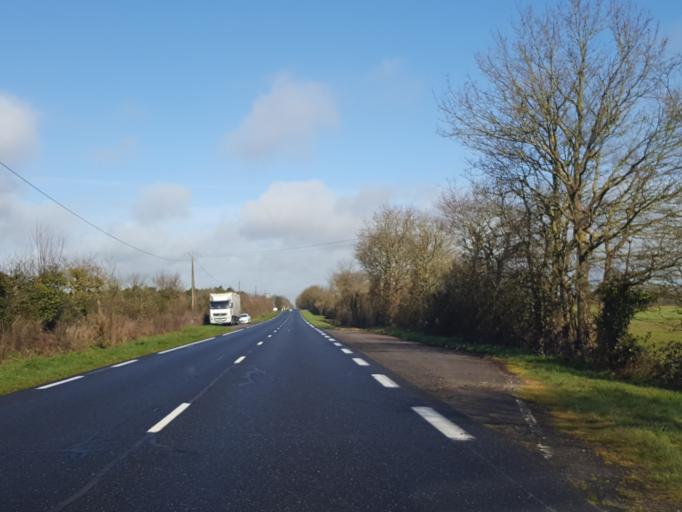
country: FR
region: Pays de la Loire
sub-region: Departement de la Vendee
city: Saligny
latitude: 46.8113
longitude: -1.4604
